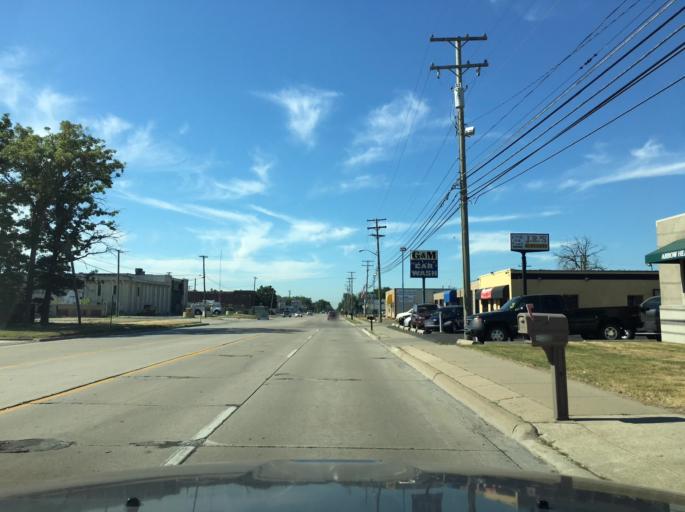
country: US
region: Michigan
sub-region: Macomb County
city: Saint Clair Shores
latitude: 42.5194
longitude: -82.9088
